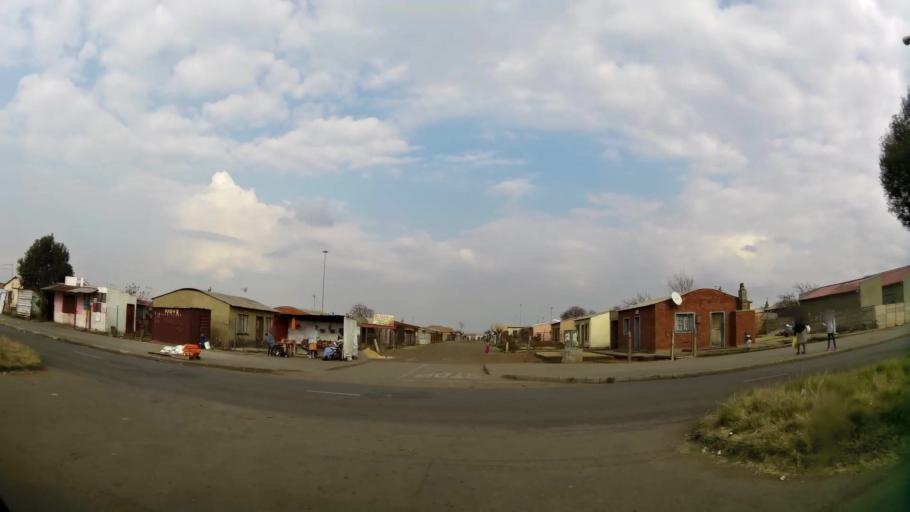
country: ZA
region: Gauteng
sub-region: Sedibeng District Municipality
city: Vanderbijlpark
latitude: -26.6842
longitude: 27.8757
